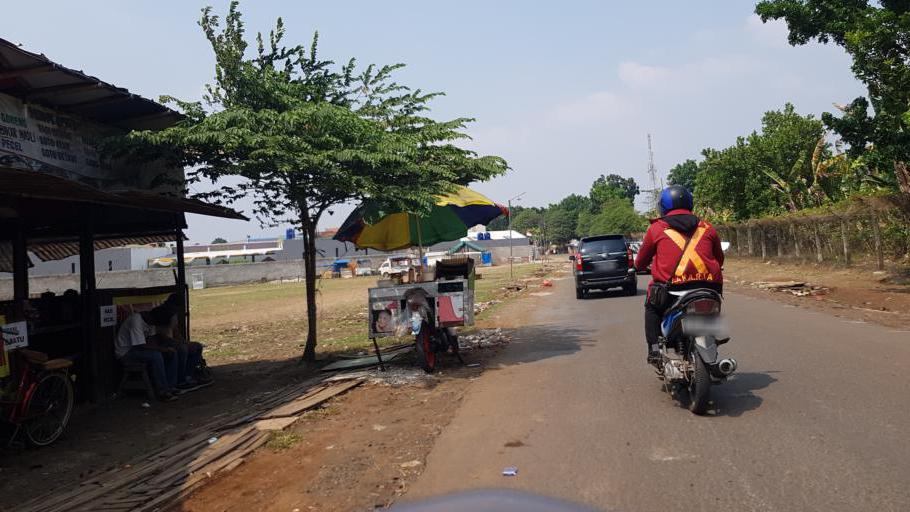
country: ID
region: West Java
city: Bekasi
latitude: -6.2858
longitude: 106.9290
